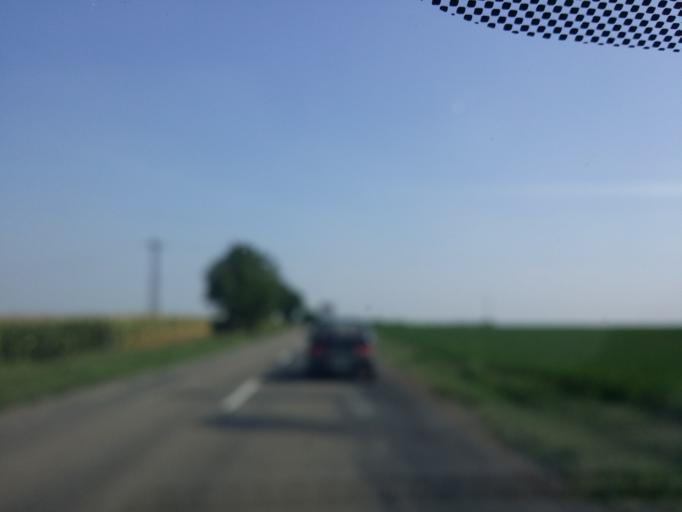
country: HU
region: Fejer
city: Mezofalva
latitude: 46.9423
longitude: 18.7462
